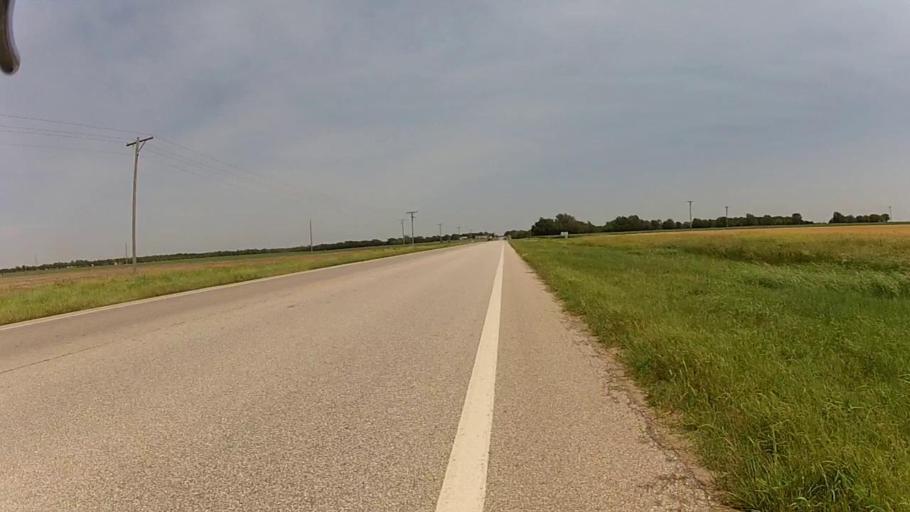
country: US
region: Kansas
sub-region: Cowley County
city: Arkansas City
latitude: 37.0565
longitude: -97.0954
